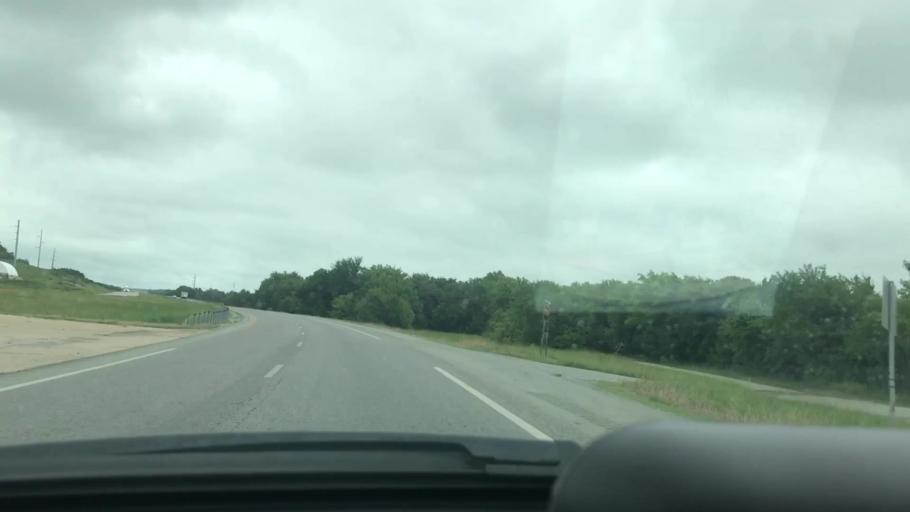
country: US
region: Oklahoma
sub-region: Coal County
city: Coalgate
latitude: 34.6476
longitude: -95.9439
